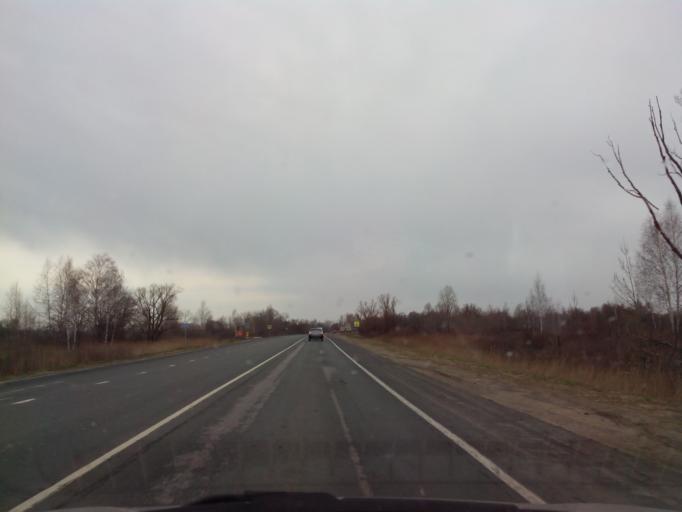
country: RU
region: Tambov
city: Michurinsk
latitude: 53.0810
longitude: 40.4117
